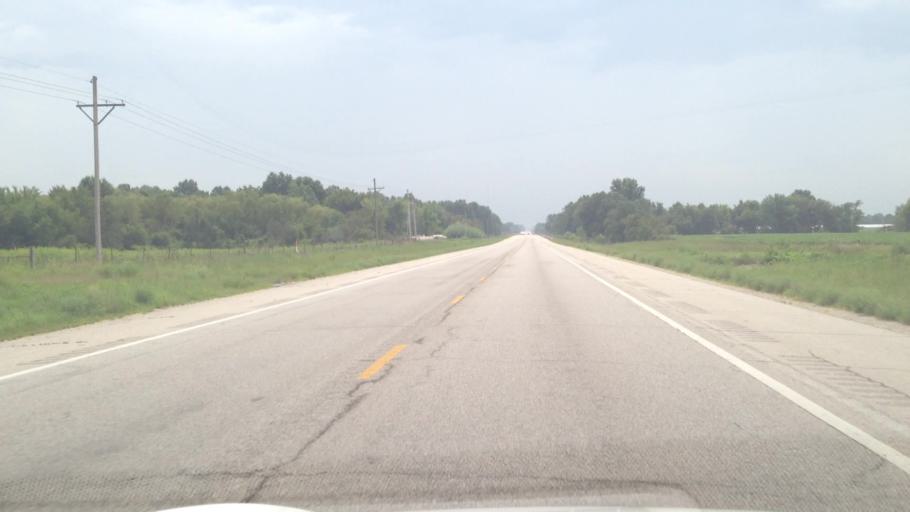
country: US
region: Kansas
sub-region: Cherokee County
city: Galena
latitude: 37.1447
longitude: -94.7044
